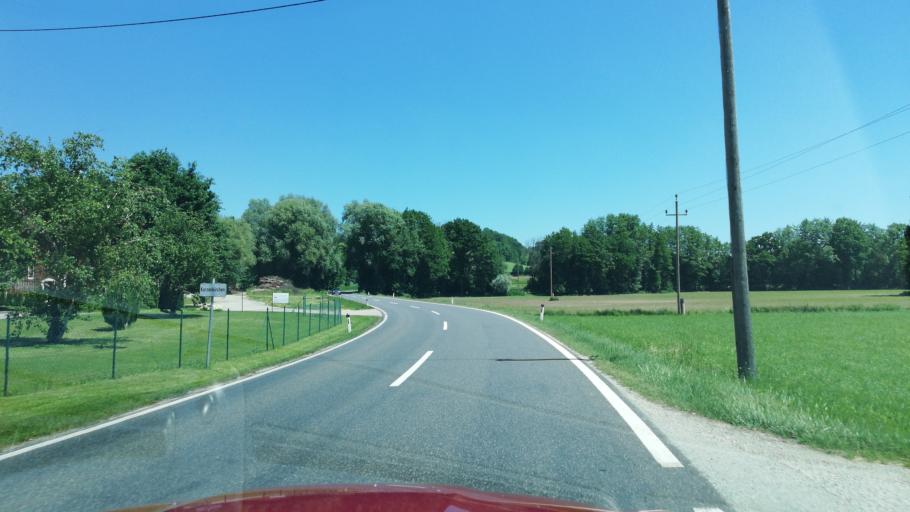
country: AT
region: Upper Austria
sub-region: Wels-Land
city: Edt bei Lambach
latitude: 48.1535
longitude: 13.8809
